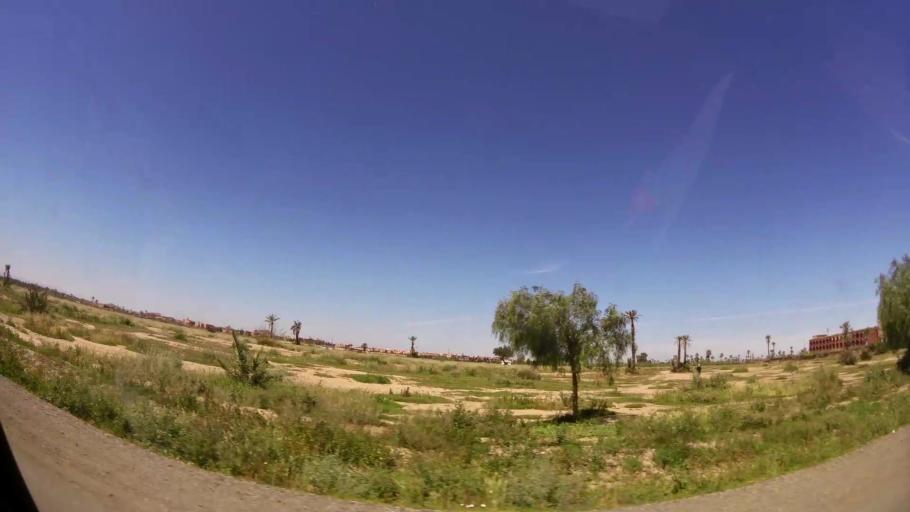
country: MA
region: Marrakech-Tensift-Al Haouz
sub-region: Marrakech
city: Marrakesh
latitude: 31.6812
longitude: -7.9914
